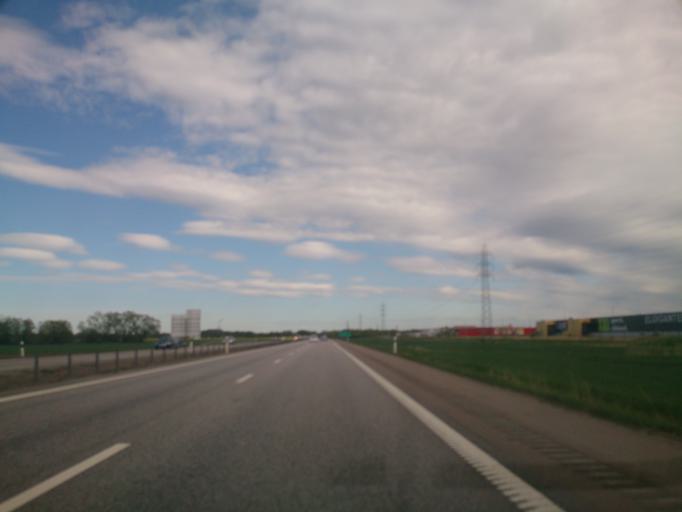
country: SE
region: OEstergoetland
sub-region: Linkopings Kommun
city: Linkoping
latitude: 58.4363
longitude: 15.5976
